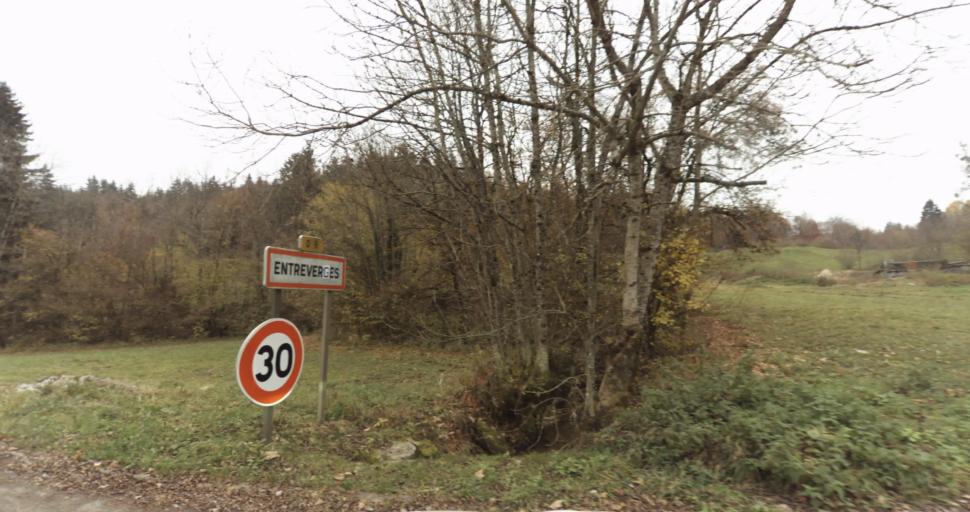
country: FR
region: Rhone-Alpes
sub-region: Departement de la Haute-Savoie
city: Doussard
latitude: 45.7894
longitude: 6.1902
